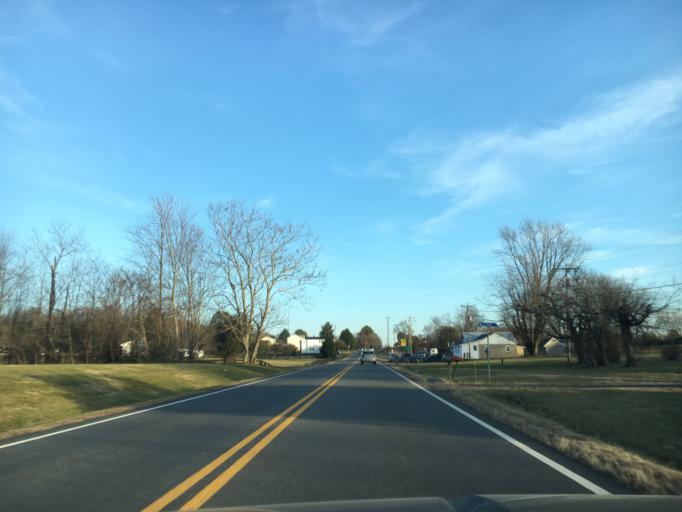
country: US
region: Virginia
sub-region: Culpeper County
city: Merrimac
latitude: 38.5135
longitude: -78.0677
